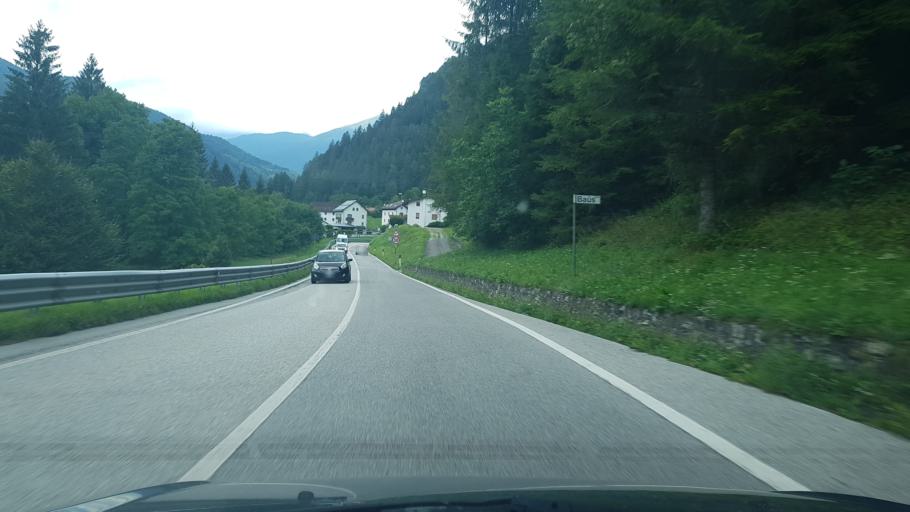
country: IT
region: Friuli Venezia Giulia
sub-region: Provincia di Udine
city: Ovaro
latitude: 46.4942
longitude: 12.8664
